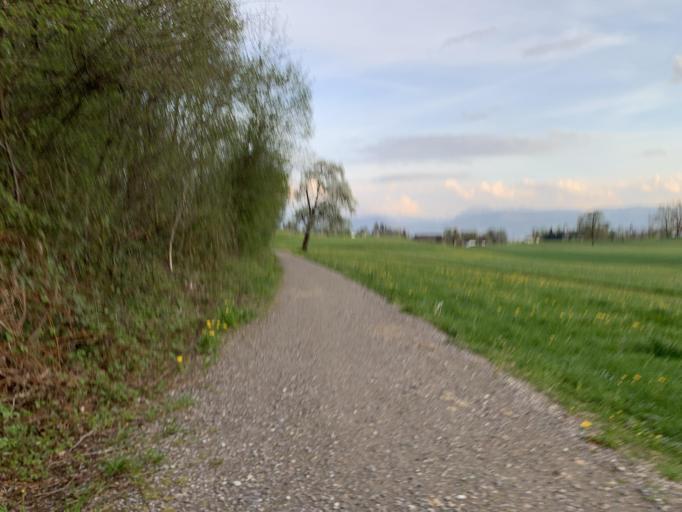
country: CH
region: Zurich
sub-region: Bezirk Hinwil
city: Hinwil
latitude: 47.2909
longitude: 8.8394
